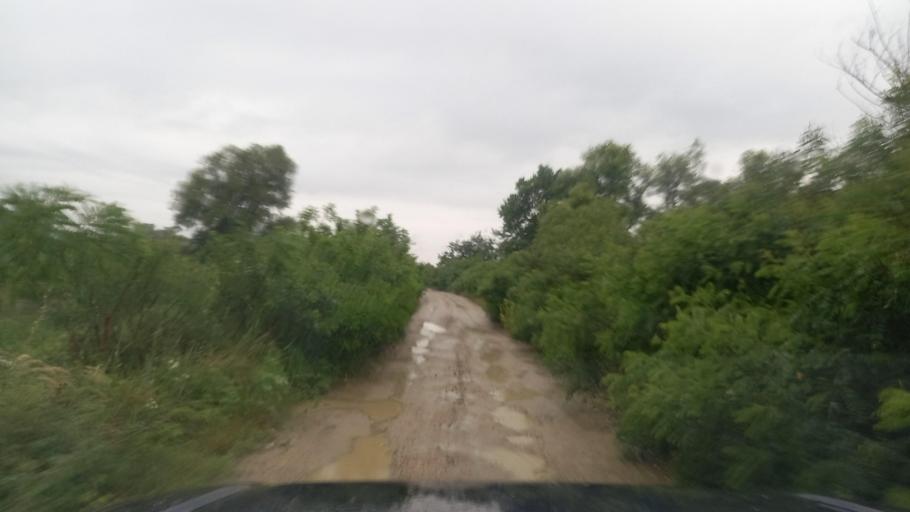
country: RU
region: Krasnodarskiy
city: Vasyurinskaya
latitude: 45.0303
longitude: 39.4752
